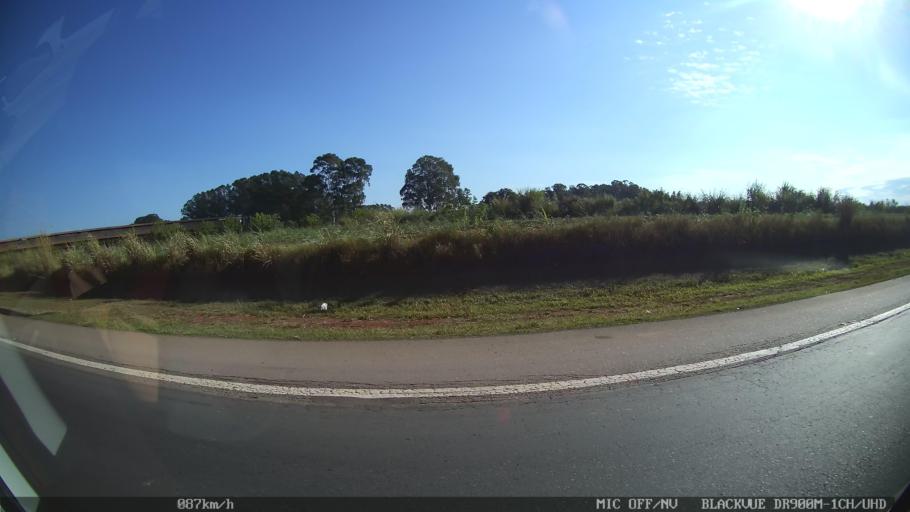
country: BR
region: Sao Paulo
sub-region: Piracicaba
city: Piracicaba
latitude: -22.7158
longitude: -47.6065
